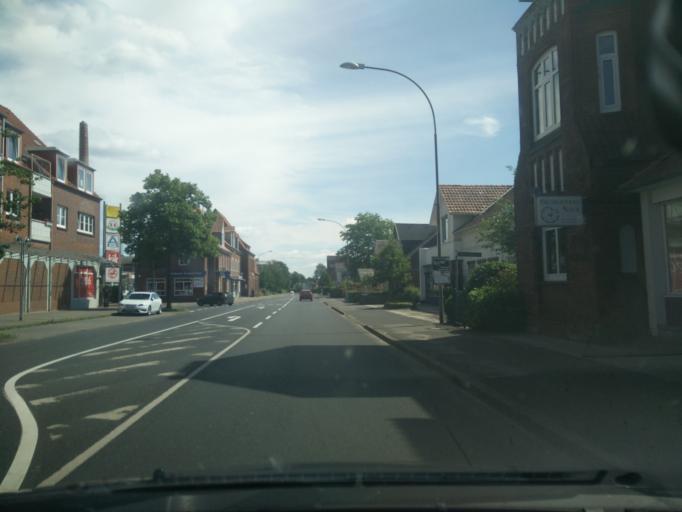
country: DE
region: Schleswig-Holstein
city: Tornesch
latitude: 53.6968
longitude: 9.7129
